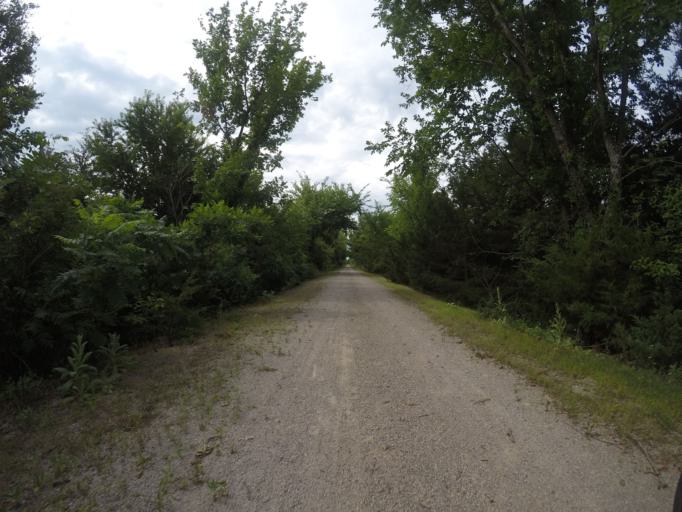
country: US
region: Kansas
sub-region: Anderson County
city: Garnett
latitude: 38.4397
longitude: -95.2642
